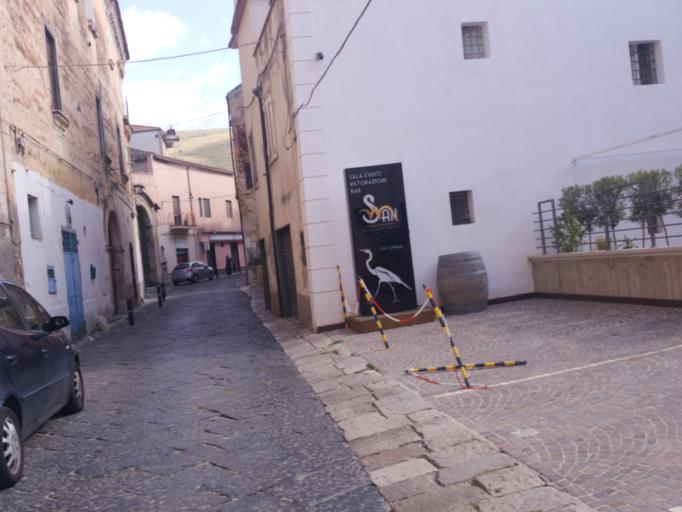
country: IT
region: Campania
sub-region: Provincia di Caserta
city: Pignataro Maggiore
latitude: 41.1909
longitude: 14.1716
